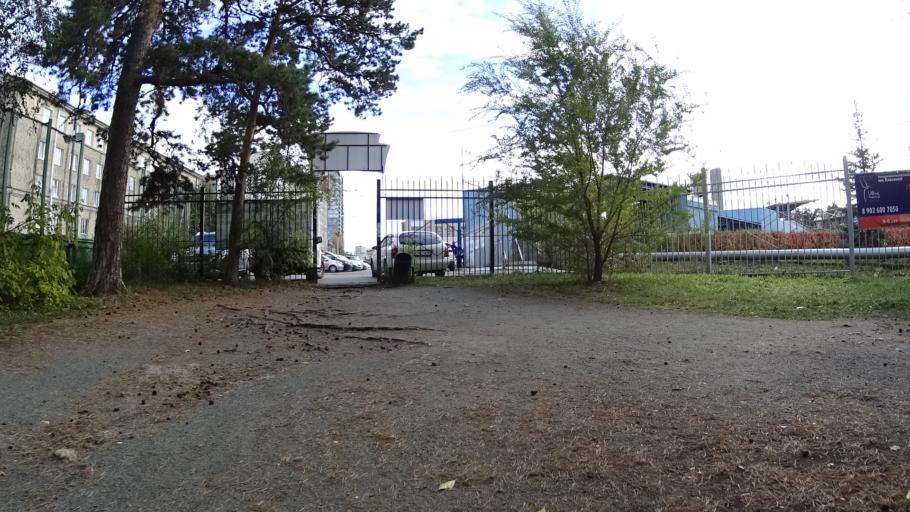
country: RU
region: Chelyabinsk
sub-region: Gorod Chelyabinsk
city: Chelyabinsk
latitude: 55.1609
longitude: 61.3642
